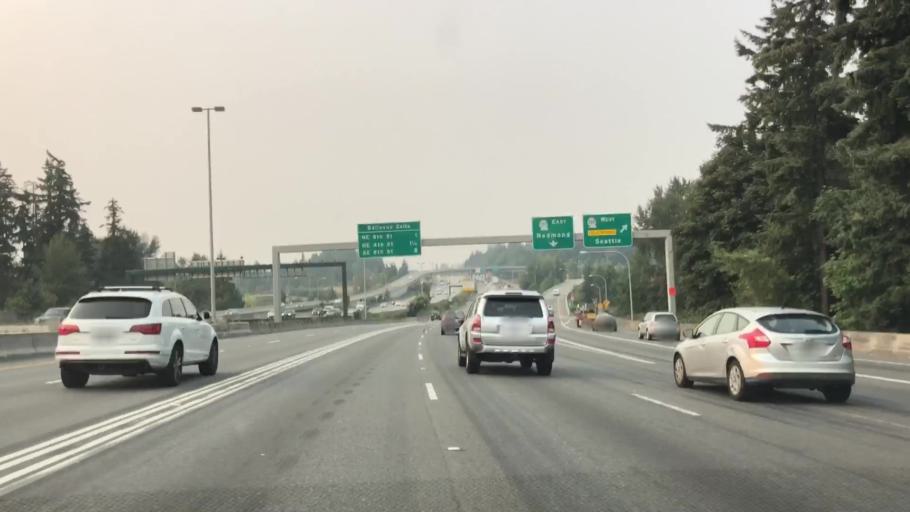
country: US
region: Washington
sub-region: King County
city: Bellevue
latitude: 47.6392
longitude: -122.1830
